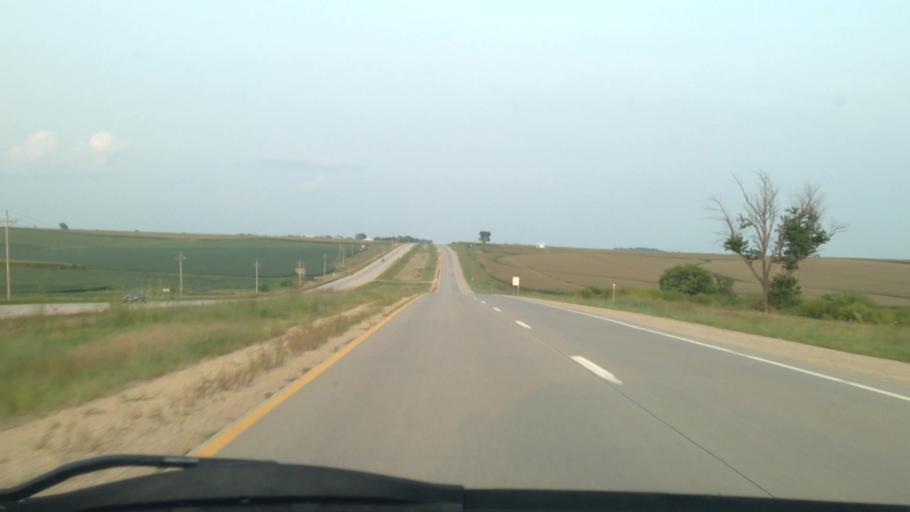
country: US
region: Iowa
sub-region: Benton County
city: Atkins
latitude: 41.9632
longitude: -91.9692
